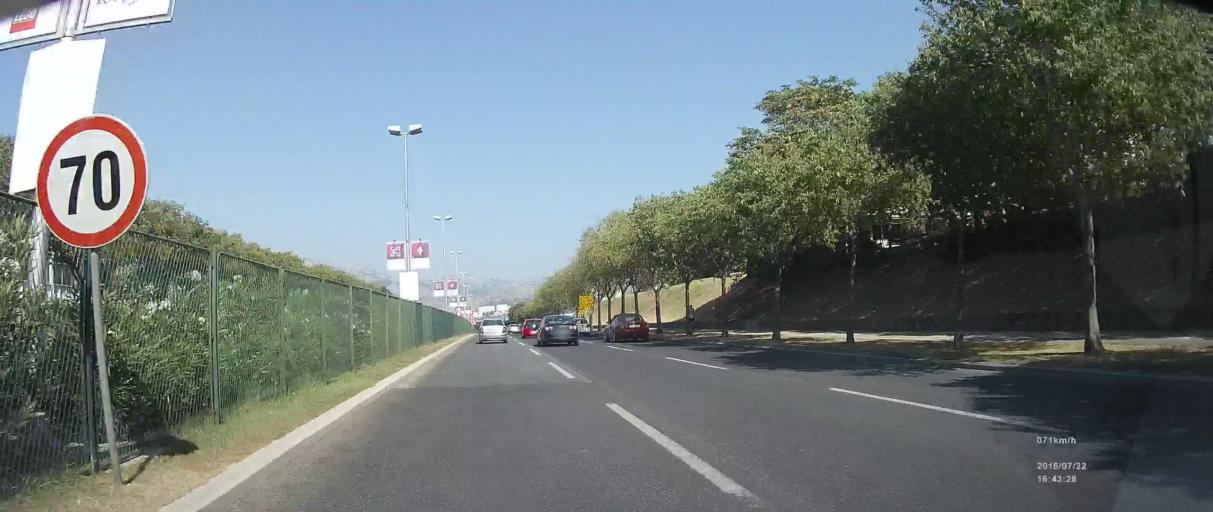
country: HR
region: Splitsko-Dalmatinska
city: Vranjic
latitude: 43.5194
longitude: 16.4701
